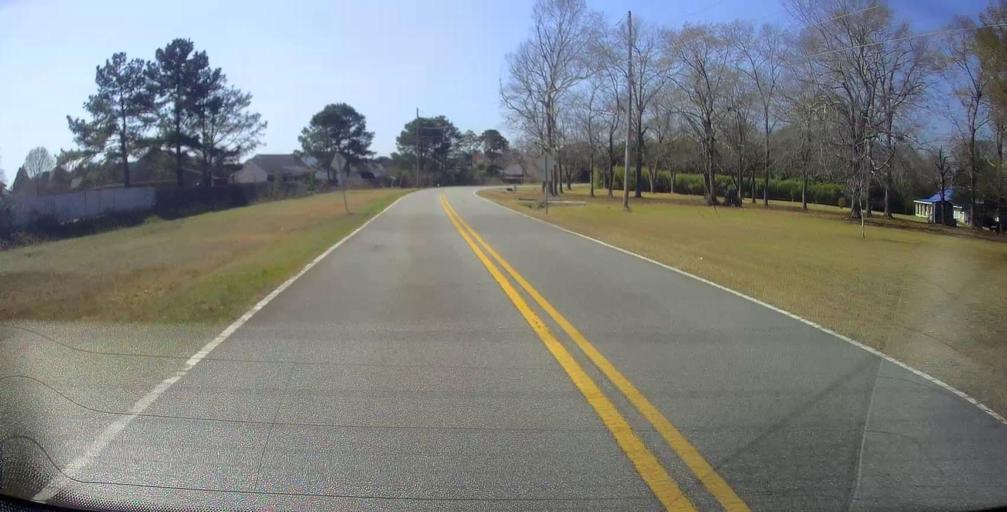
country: US
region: Georgia
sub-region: Houston County
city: Centerville
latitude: 32.5853
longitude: -83.6961
